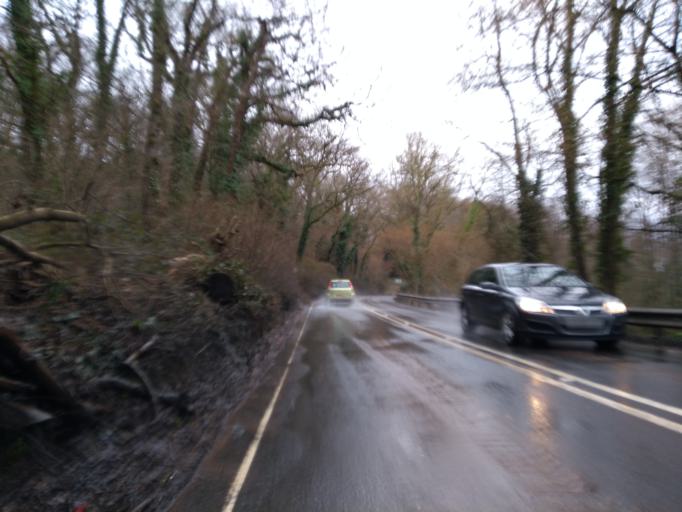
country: GB
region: England
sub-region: Devon
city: Exeter
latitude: 50.7621
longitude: -3.5107
